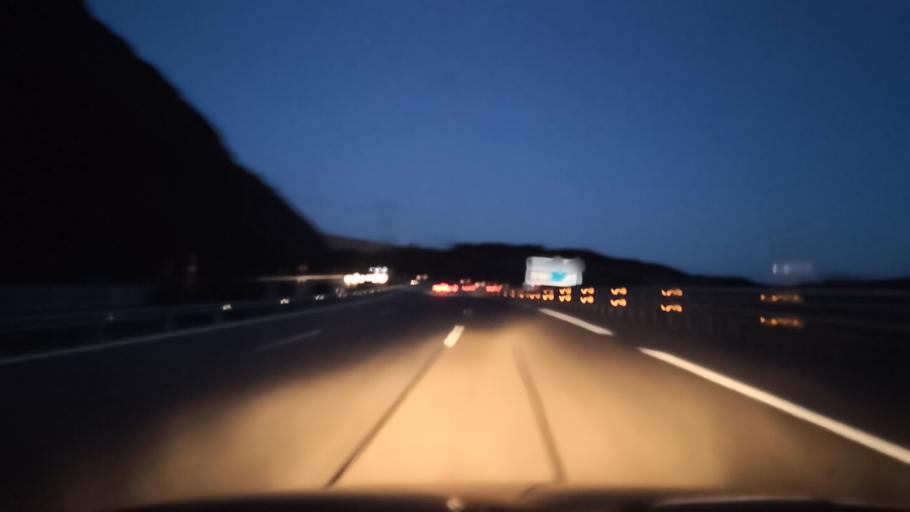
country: ES
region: Castille and Leon
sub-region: Provincia de Leon
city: Folgoso de la Ribera
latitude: 42.6051
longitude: -6.2509
